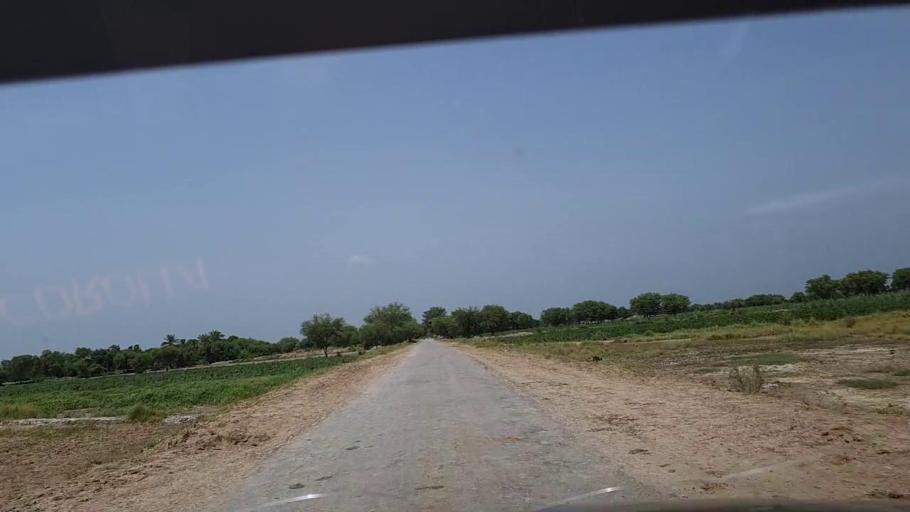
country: PK
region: Sindh
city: Khanpur
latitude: 27.7944
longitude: 69.4547
